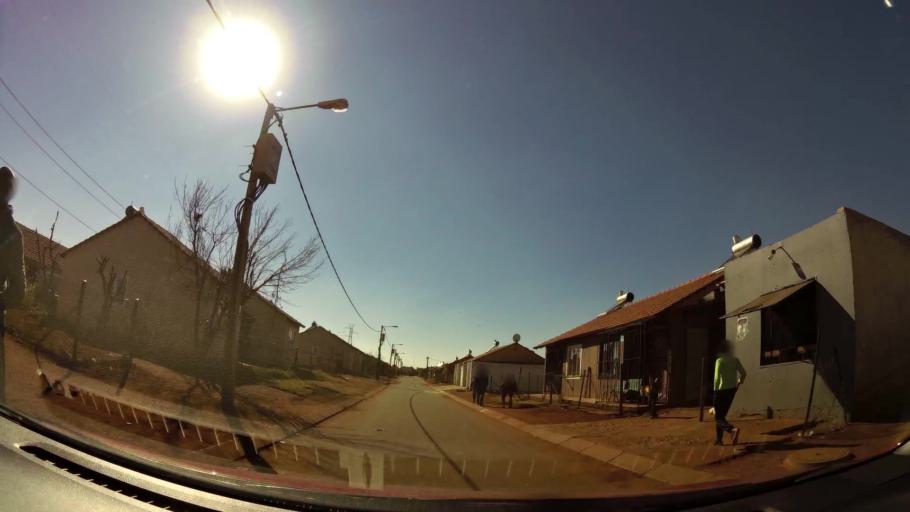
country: ZA
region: Gauteng
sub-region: City of Johannesburg Metropolitan Municipality
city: Soweto
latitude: -26.2336
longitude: 27.7989
